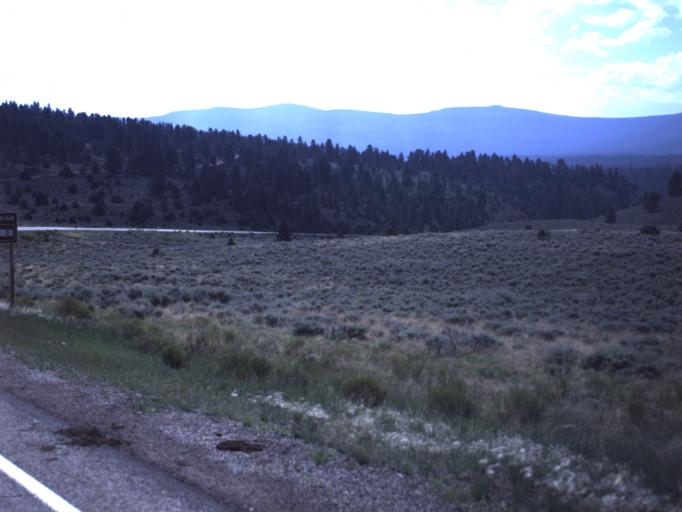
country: US
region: Utah
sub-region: Daggett County
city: Manila
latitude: 40.8832
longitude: -109.6953
